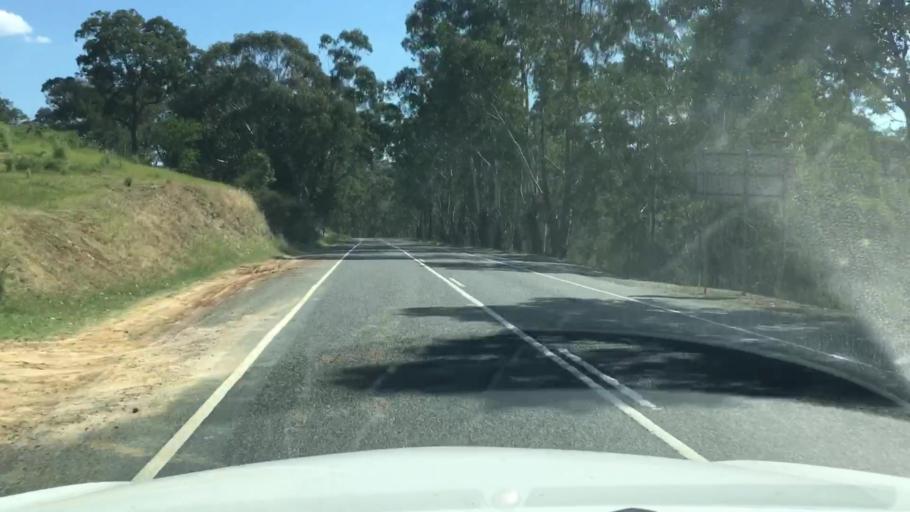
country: AU
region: Victoria
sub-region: Nillumbik
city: Saint Andrews
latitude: -37.6577
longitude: 145.2732
